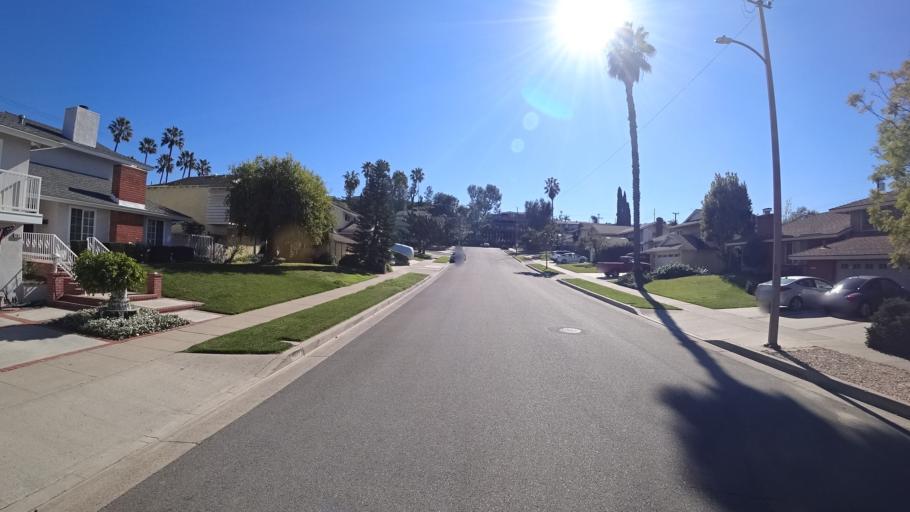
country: US
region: California
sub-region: Orange County
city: Villa Park
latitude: 33.8436
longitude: -117.8381
